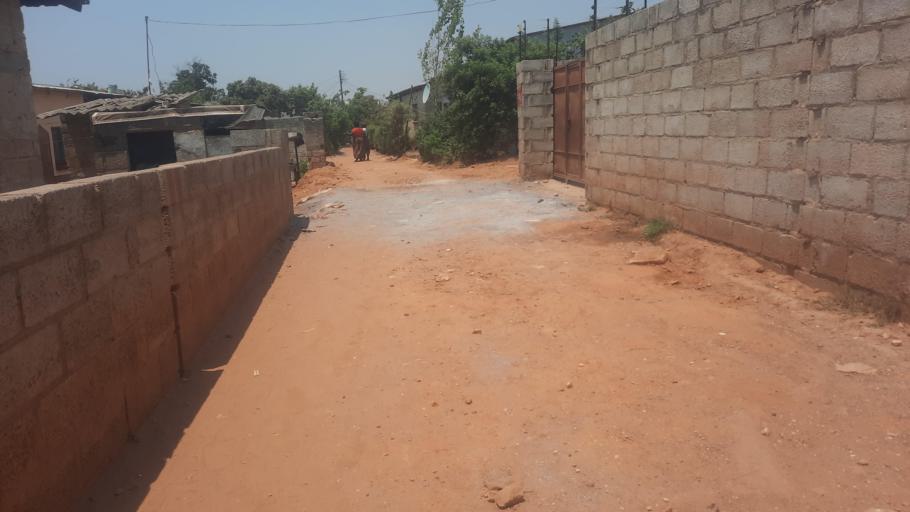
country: ZM
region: Lusaka
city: Lusaka
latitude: -15.4014
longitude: 28.3714
